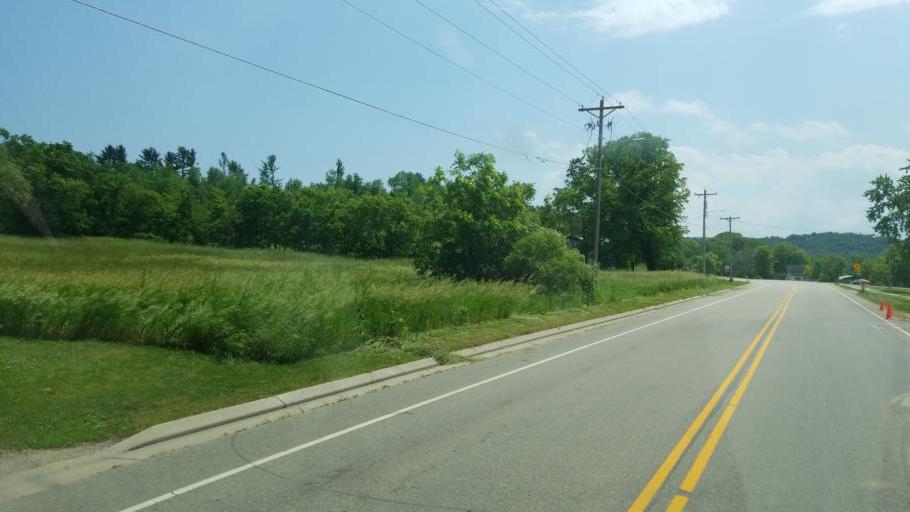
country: US
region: Wisconsin
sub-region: Vernon County
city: Viroqua
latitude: 43.5020
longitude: -90.6795
